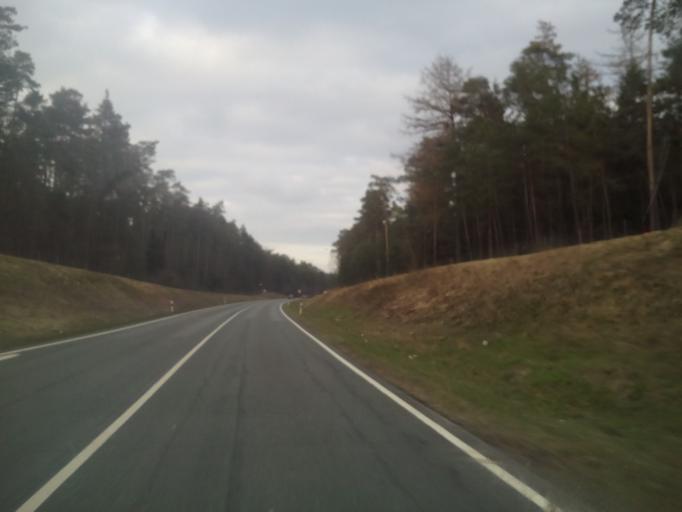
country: DE
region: Bavaria
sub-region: Upper Franconia
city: Pommersfelden
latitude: 49.7462
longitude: 10.8300
